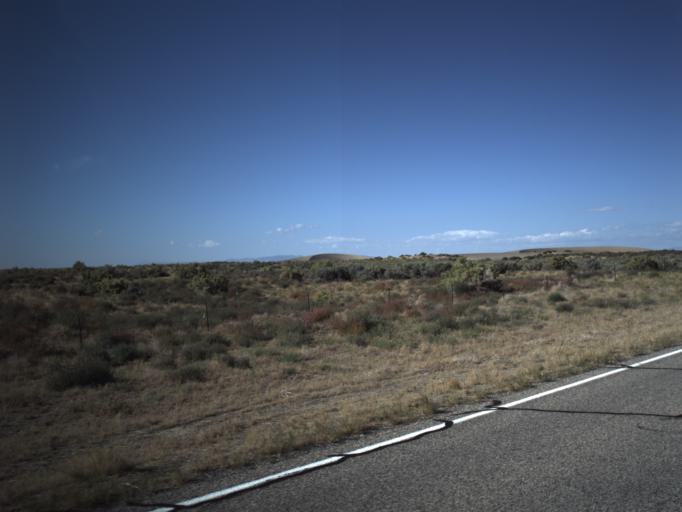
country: US
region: Utah
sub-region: Millard County
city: Delta
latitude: 39.3546
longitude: -112.3955
